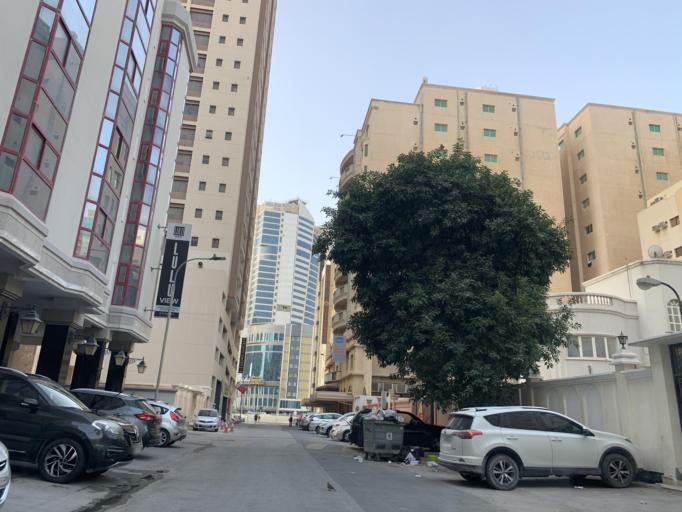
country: BH
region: Manama
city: Manama
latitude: 26.2184
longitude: 50.6095
